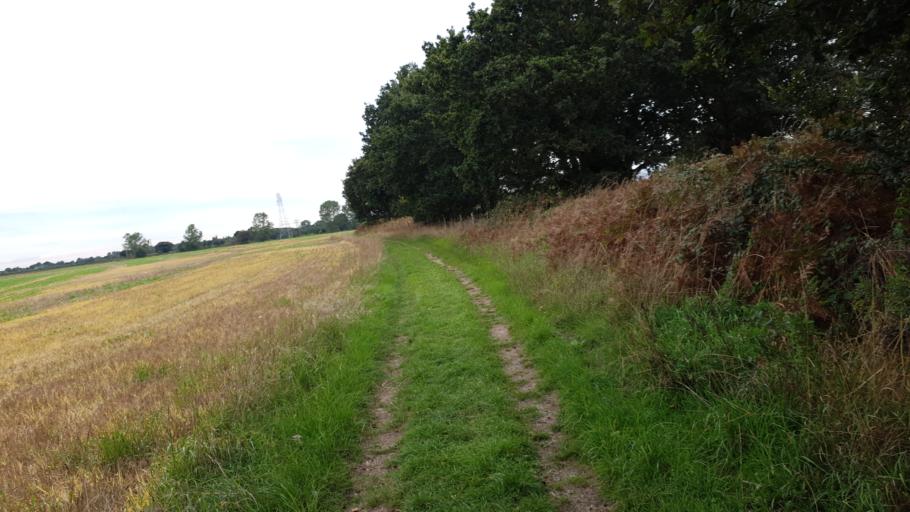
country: GB
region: England
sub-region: Essex
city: Manningtree
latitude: 51.9432
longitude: 1.0303
